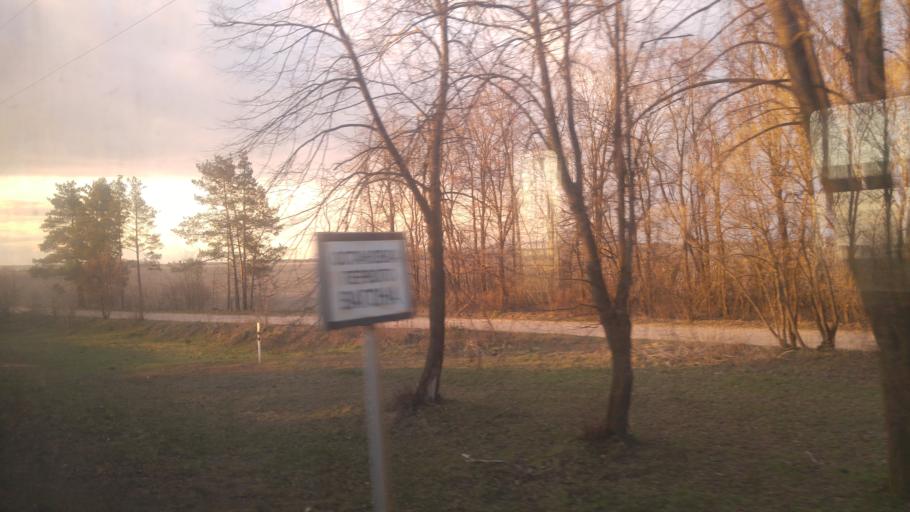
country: BY
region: Minsk
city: Rudzyensk
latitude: 53.6423
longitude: 27.7890
